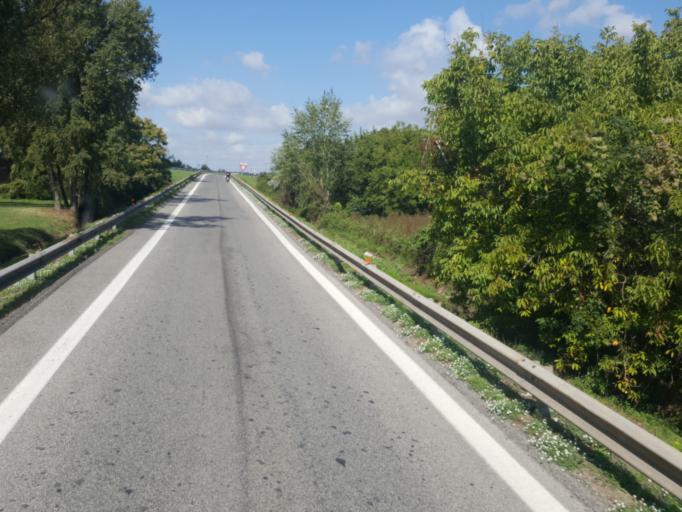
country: IT
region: Campania
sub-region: Provincia di Napoli
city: San Vitaliano
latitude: 40.9377
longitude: 14.4947
